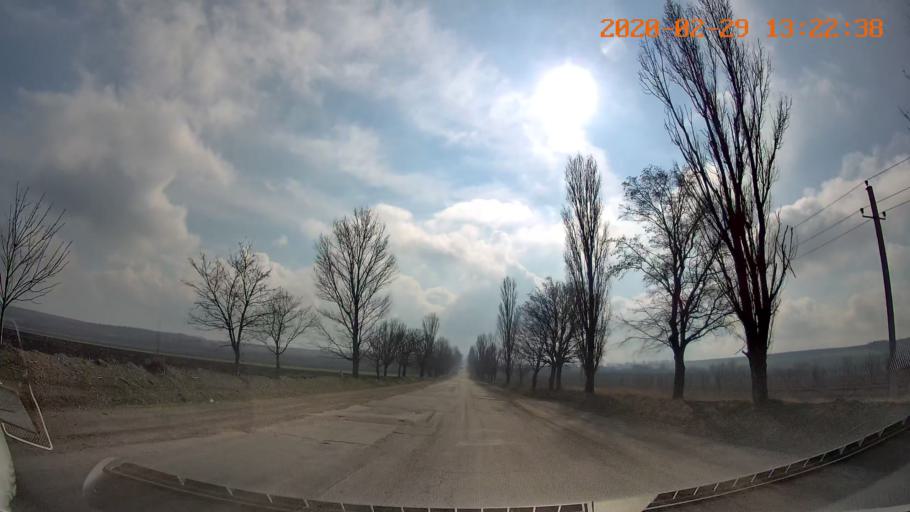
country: MD
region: Telenesti
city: Camenca
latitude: 47.9583
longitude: 28.6274
